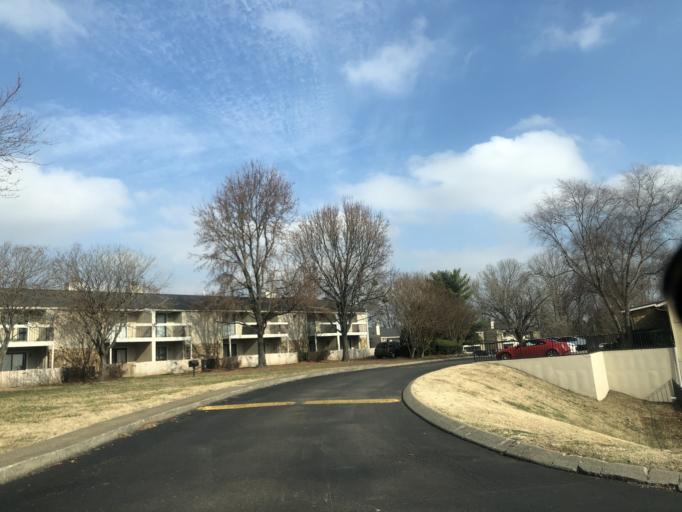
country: US
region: Tennessee
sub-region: Davidson County
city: Oak Hill
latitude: 36.1014
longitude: -86.7164
